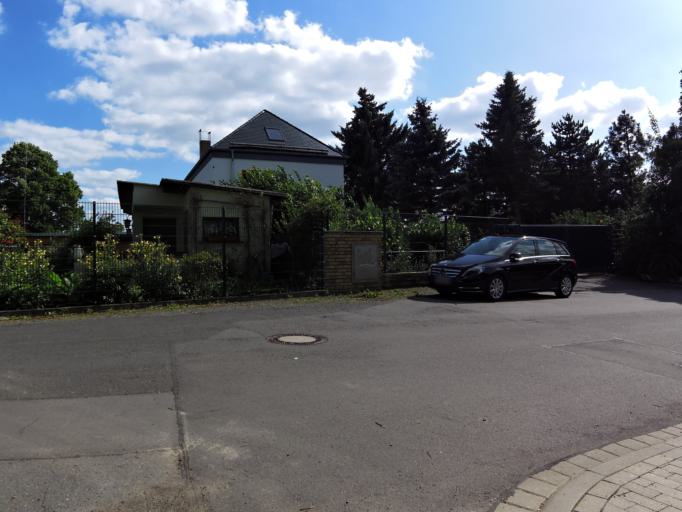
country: DE
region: Saxony
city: Leipzig
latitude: 51.3358
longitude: 12.4276
